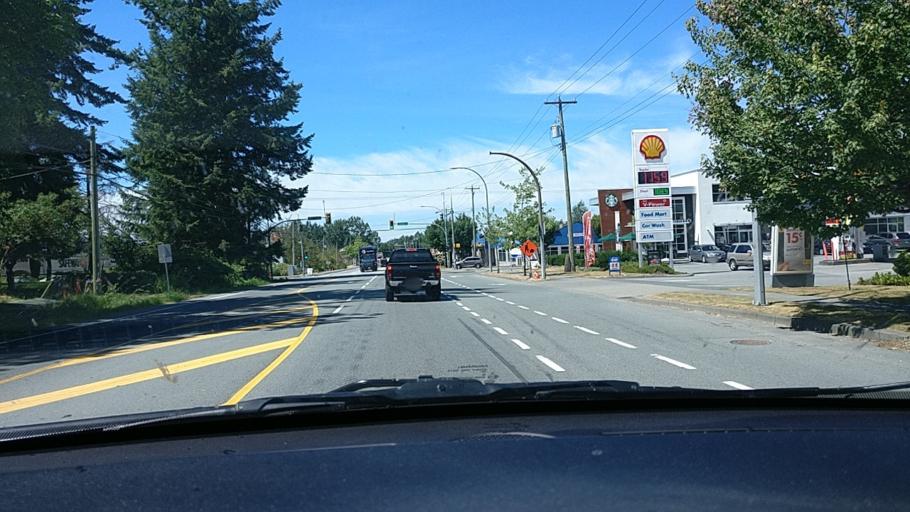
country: CA
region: British Columbia
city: Aldergrove
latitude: 49.0576
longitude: -122.4585
